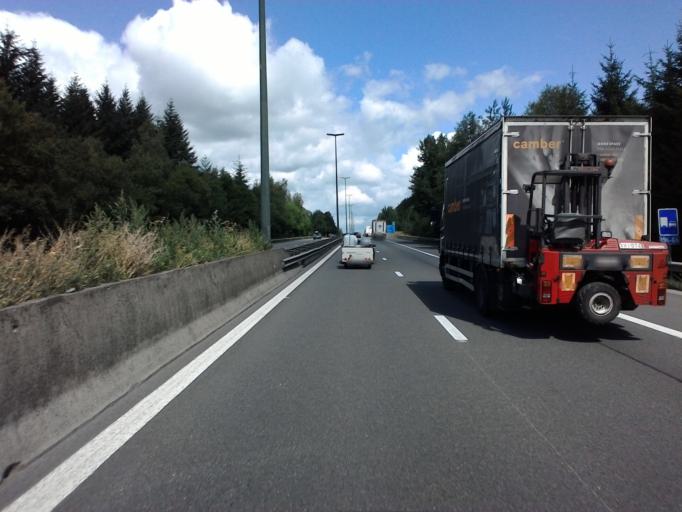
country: BE
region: Wallonia
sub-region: Province du Luxembourg
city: Leglise
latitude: 49.7538
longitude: 5.5659
